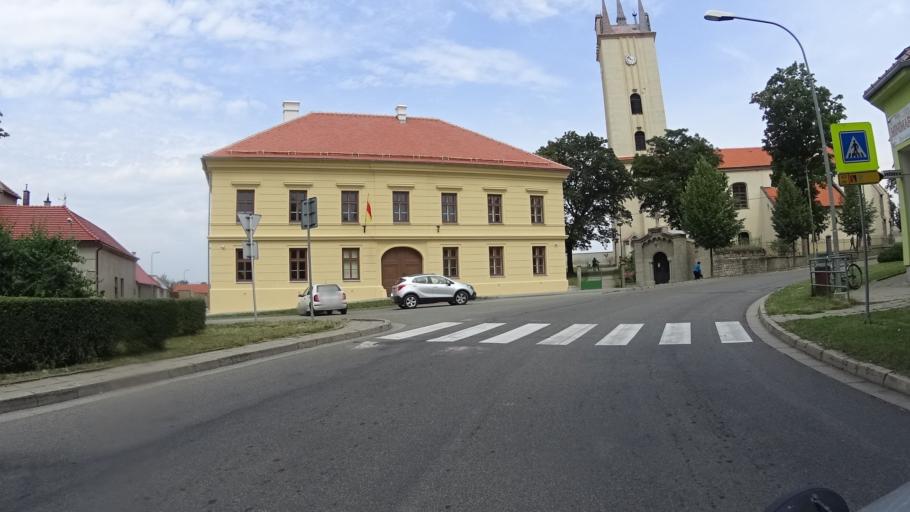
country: CZ
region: South Moravian
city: Podivin
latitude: 48.8258
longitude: 16.8462
